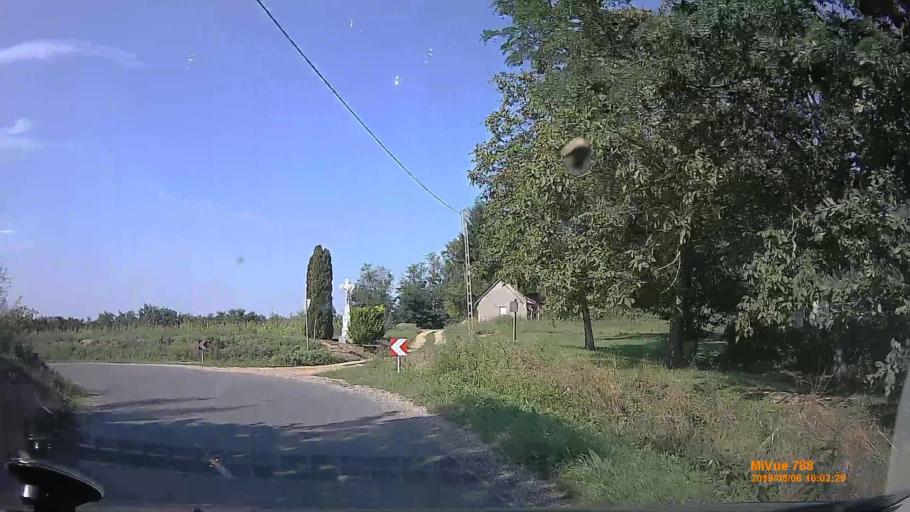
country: HU
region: Zala
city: Murakeresztur
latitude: 46.3035
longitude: 16.9750
